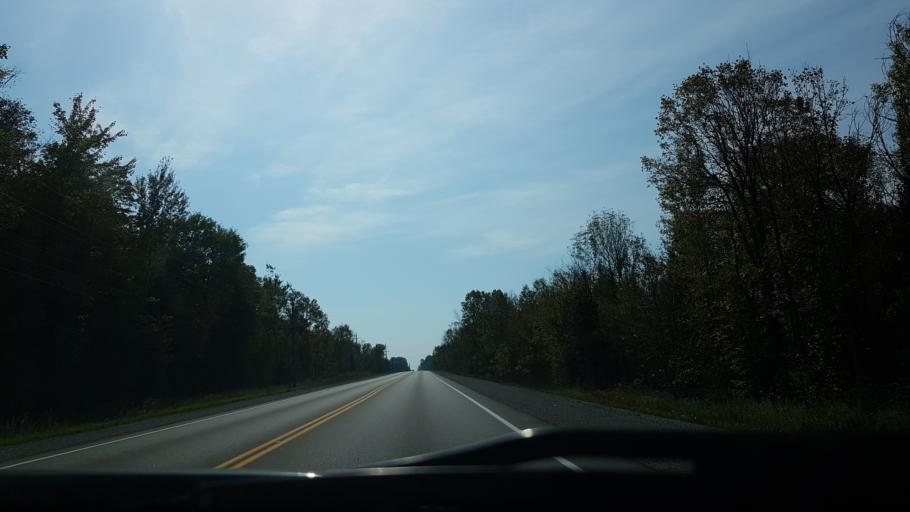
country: CA
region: Ontario
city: Orillia
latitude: 44.7368
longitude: -79.2913
